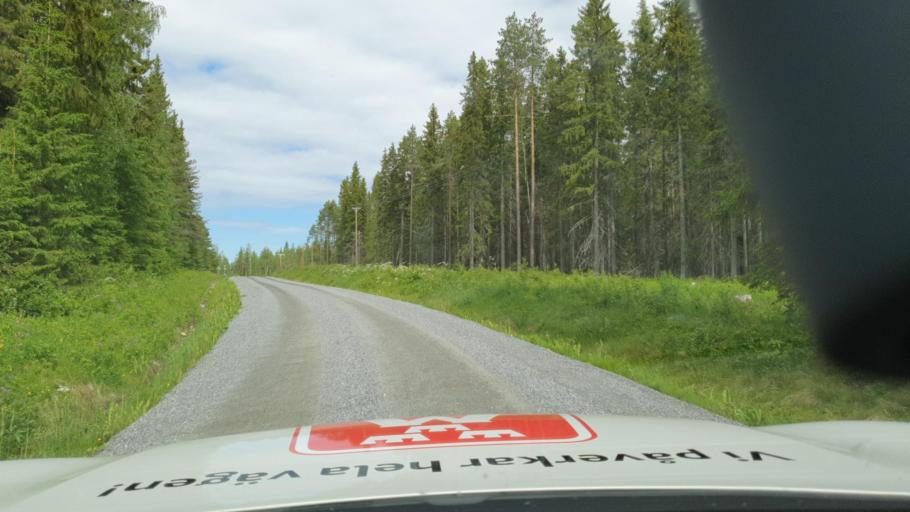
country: SE
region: Vaesterbotten
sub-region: Skelleftea Kommun
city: Langsele
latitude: 64.5973
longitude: 20.2954
